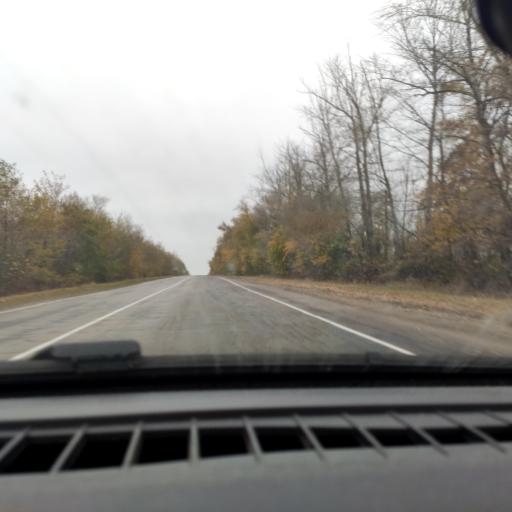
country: RU
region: Voronezj
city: Uryv-Pokrovka
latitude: 51.1426
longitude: 39.0563
